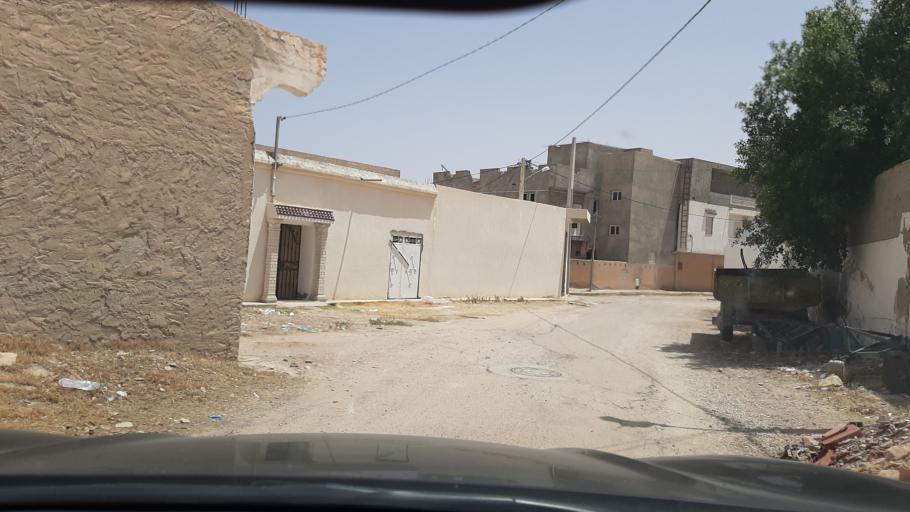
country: TN
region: Qabis
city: Matmata
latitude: 33.6188
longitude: 10.2823
